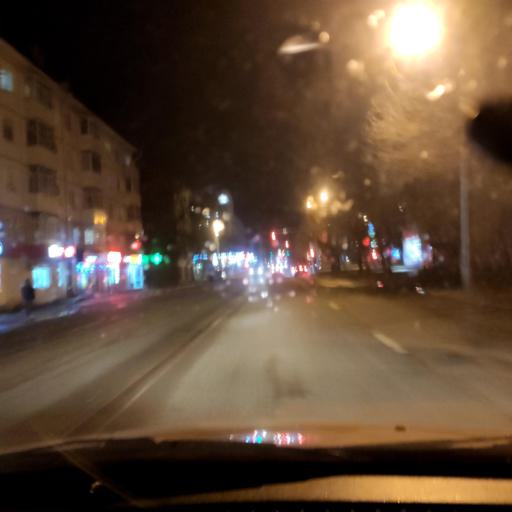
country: RU
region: Bashkortostan
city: Ufa
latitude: 54.7598
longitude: 56.0126
